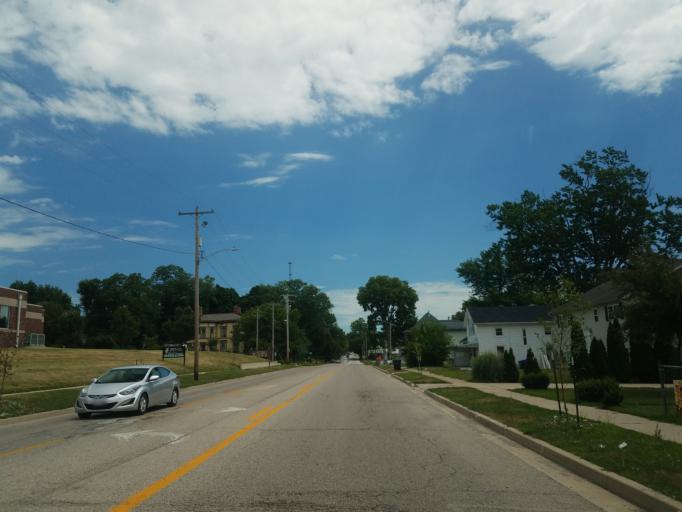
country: US
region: Illinois
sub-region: McLean County
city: Bloomington
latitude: 40.4821
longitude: -89.0032
